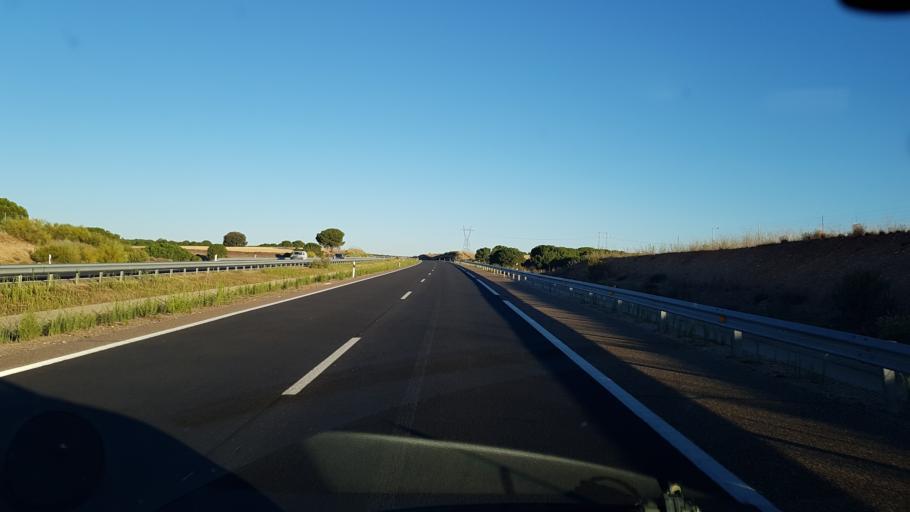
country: ES
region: Castille and Leon
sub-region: Provincia de Zamora
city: Toro
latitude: 41.5456
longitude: -5.4242
